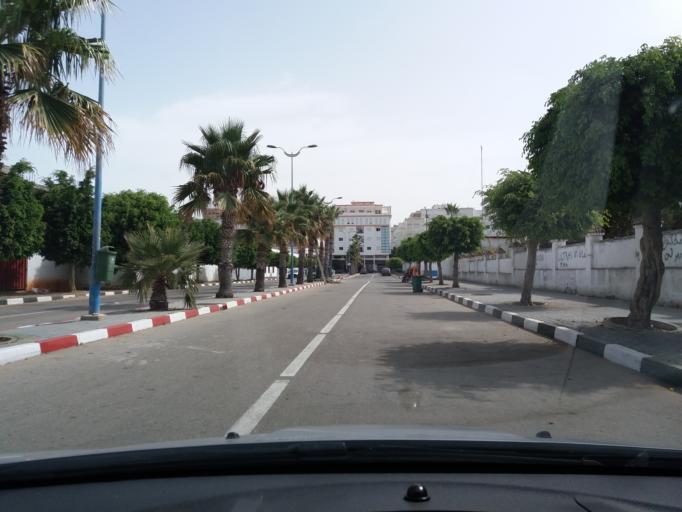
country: MA
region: Tanger-Tetouan
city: Asilah
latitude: 35.4694
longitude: -6.0316
